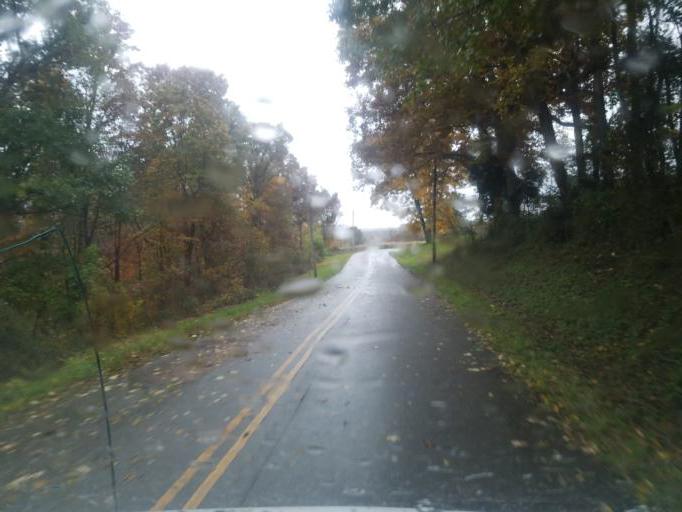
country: US
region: Ohio
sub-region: Washington County
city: Beverly
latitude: 39.4586
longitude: -81.6215
